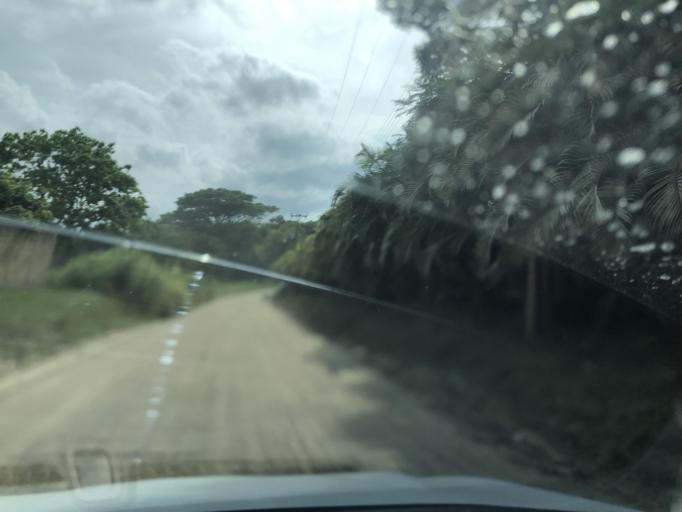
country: BR
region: Santa Catarina
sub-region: Sao Francisco Do Sul
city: Sao Francisco do Sul
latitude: -26.2281
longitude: -48.5856
